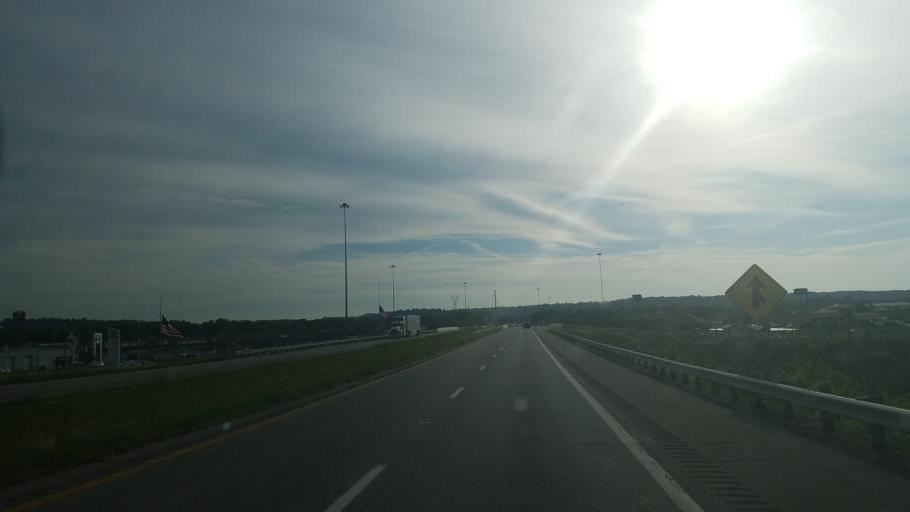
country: US
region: Ohio
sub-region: Ross County
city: Chillicothe
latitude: 39.3488
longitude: -82.9738
